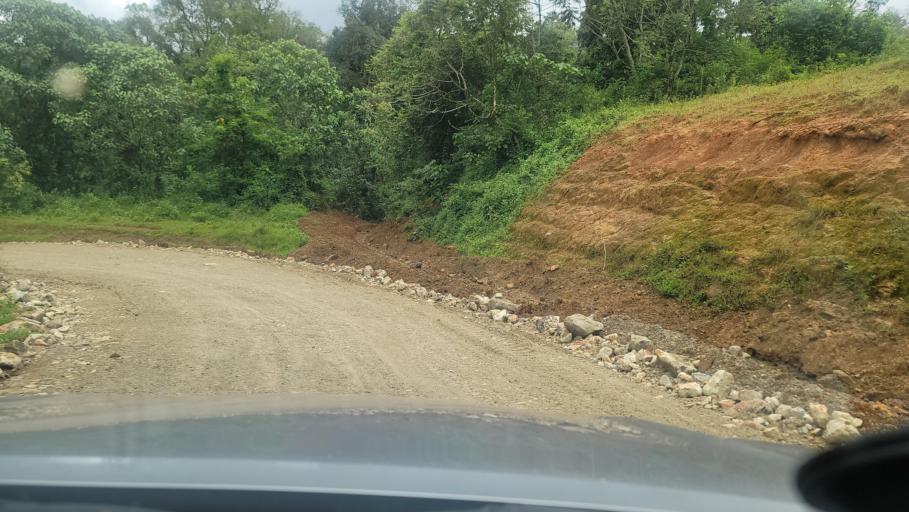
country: ET
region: Southern Nations, Nationalities, and People's Region
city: Bonga
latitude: 7.6180
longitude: 36.2081
